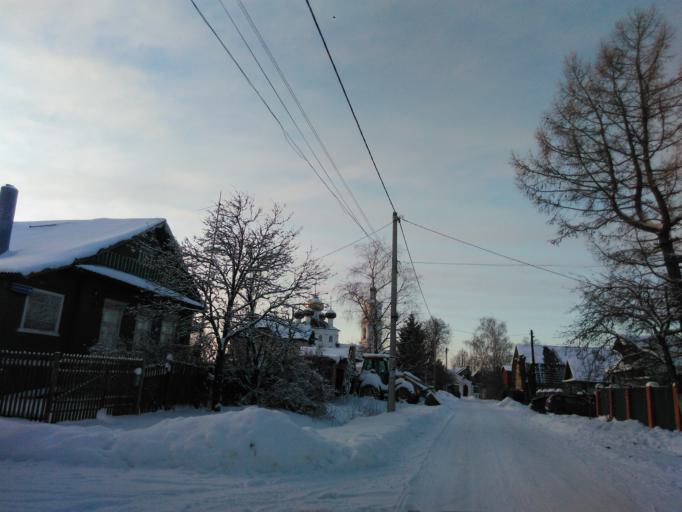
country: RU
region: Tverskaya
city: Zavidovo
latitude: 56.6347
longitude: 36.6149
